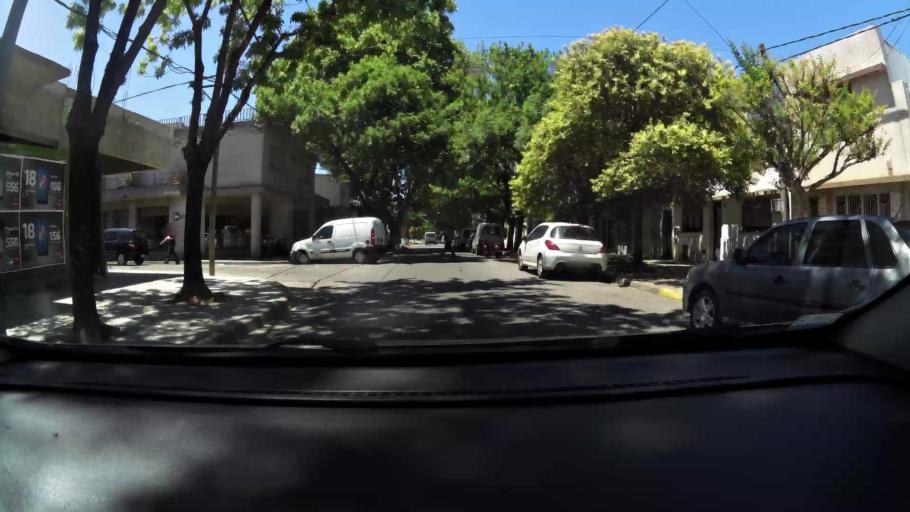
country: AR
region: Santa Fe
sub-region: Departamento de Rosario
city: Rosario
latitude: -32.9470
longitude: -60.6979
